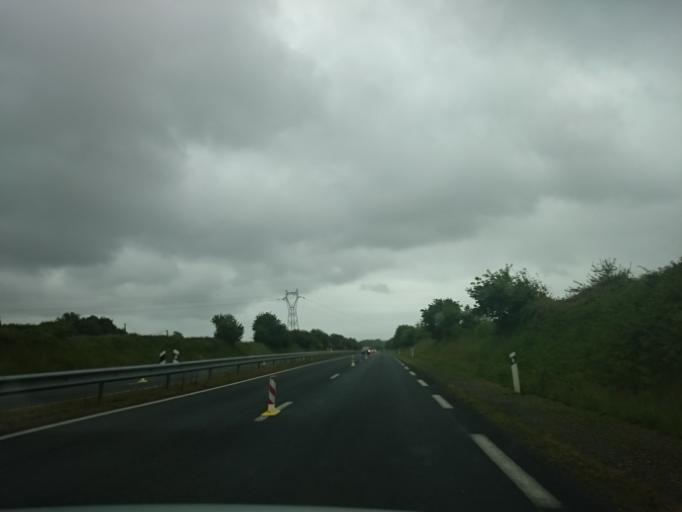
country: FR
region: Brittany
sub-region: Departement des Cotes-d'Armor
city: Pedernec
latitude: 48.5793
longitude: -3.2300
